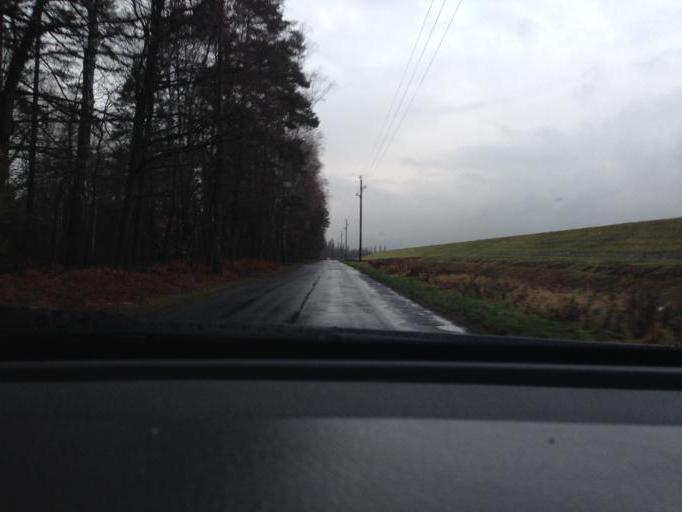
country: PL
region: Opole Voivodeship
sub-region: Powiat opolski
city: Chrzastowice
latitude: 50.7128
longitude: 18.0893
